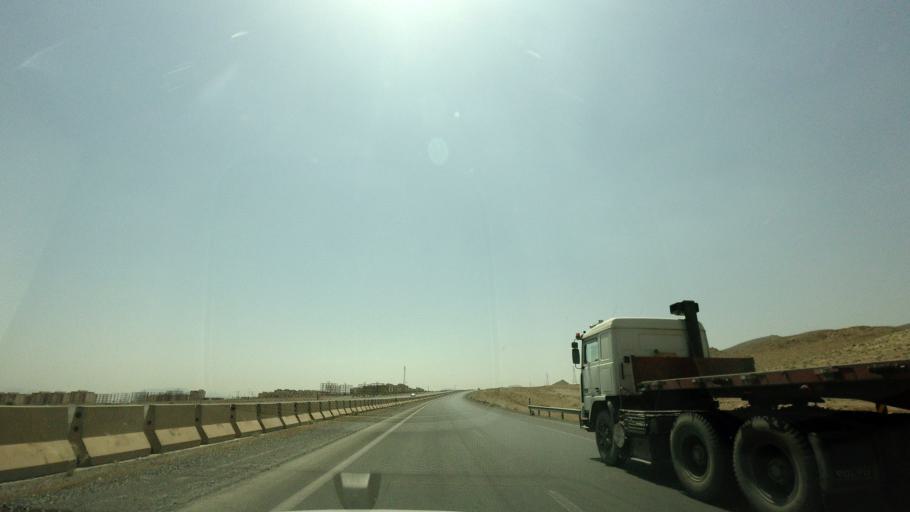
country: IR
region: Isfahan
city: Najafabad
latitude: 32.5317
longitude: 51.3338
